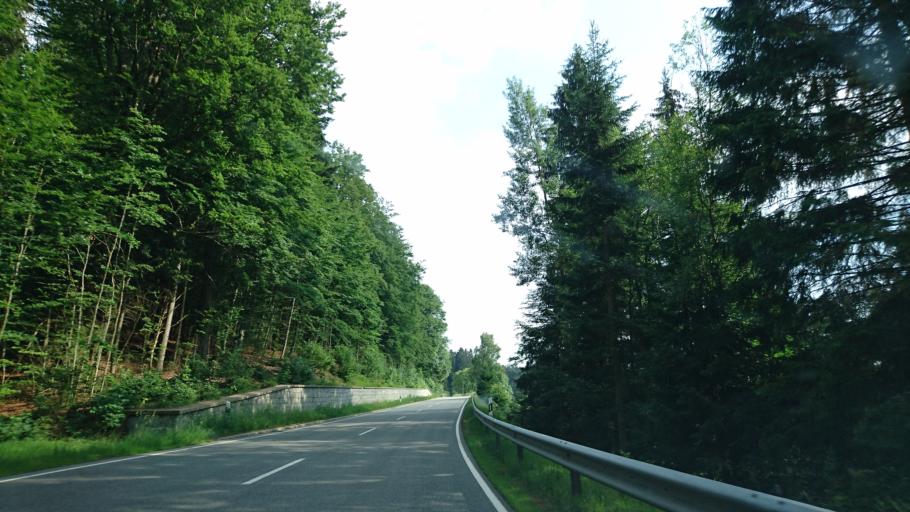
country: DE
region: Bavaria
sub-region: Lower Bavaria
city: Neuschonau
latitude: 48.9086
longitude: 13.4679
